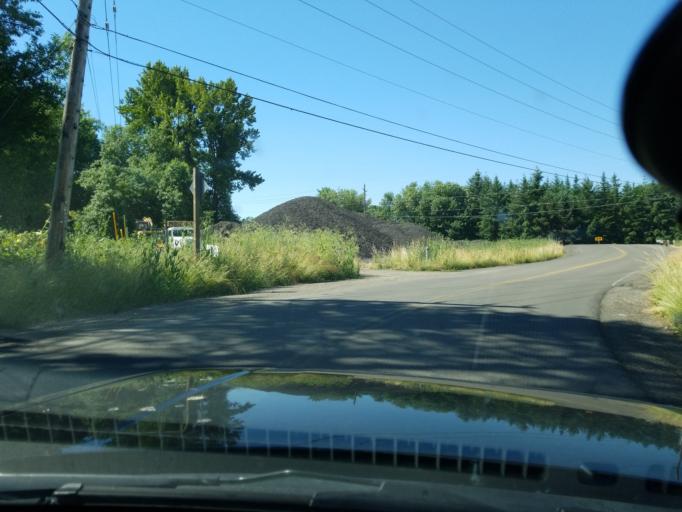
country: US
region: Oregon
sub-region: Yamhill County
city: McMinnville
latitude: 45.2309
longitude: -123.2311
